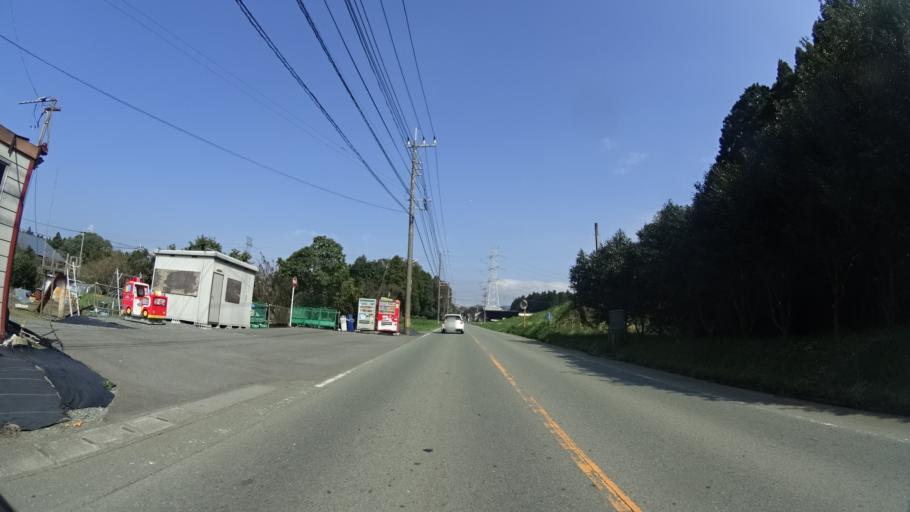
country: JP
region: Kumamoto
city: Ozu
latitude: 32.8899
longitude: 130.9032
